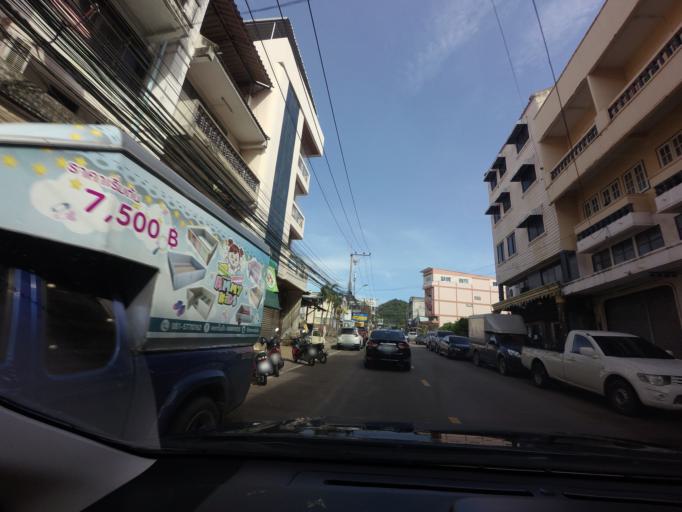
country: TH
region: Chon Buri
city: Si Racha
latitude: 13.1598
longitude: 100.9204
